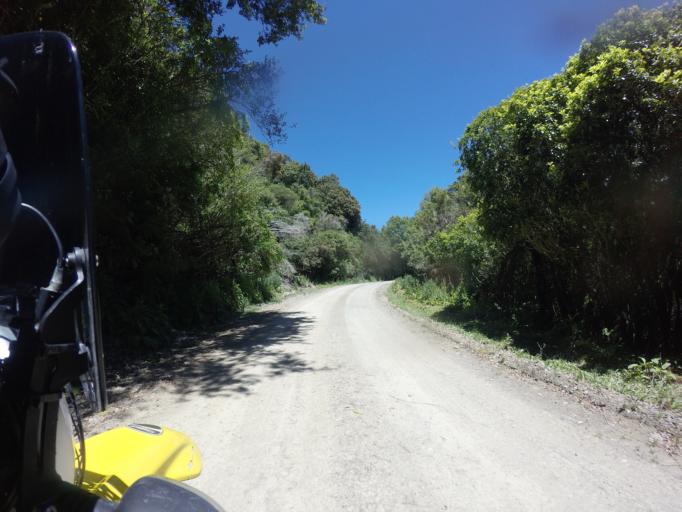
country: NZ
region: Bay of Plenty
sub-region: Opotiki District
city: Opotiki
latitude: -38.4088
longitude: 177.4175
